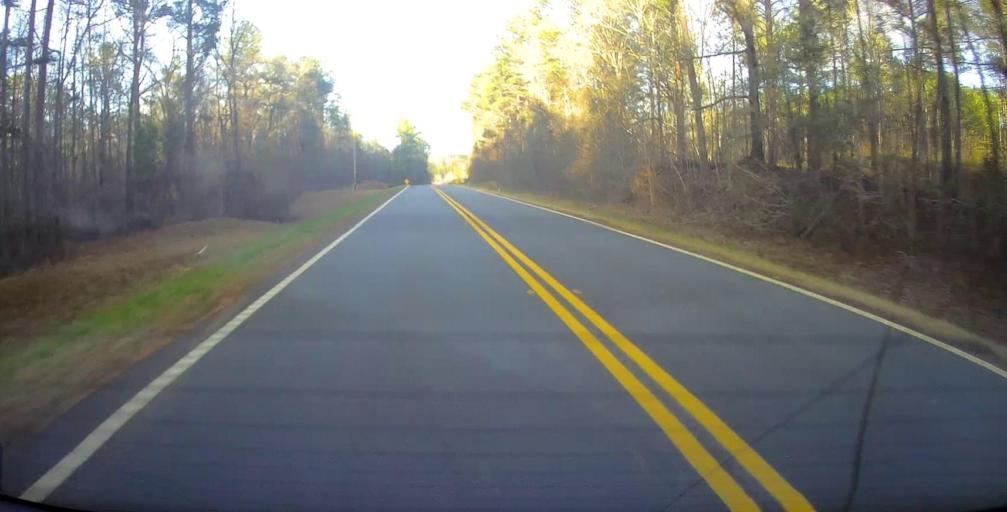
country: US
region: Georgia
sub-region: Talbot County
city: Sardis
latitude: 32.7571
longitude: -84.5691
